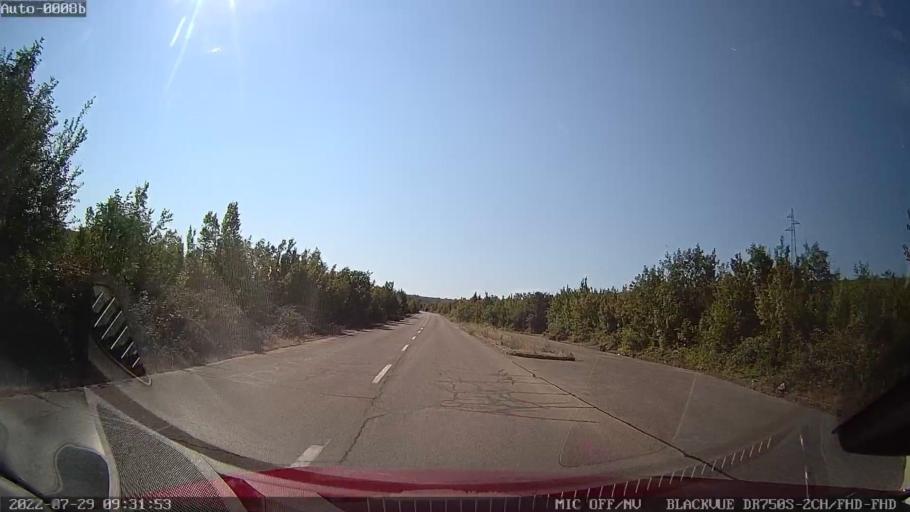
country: HR
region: Zadarska
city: Obrovac
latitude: 44.1858
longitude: 15.7045
